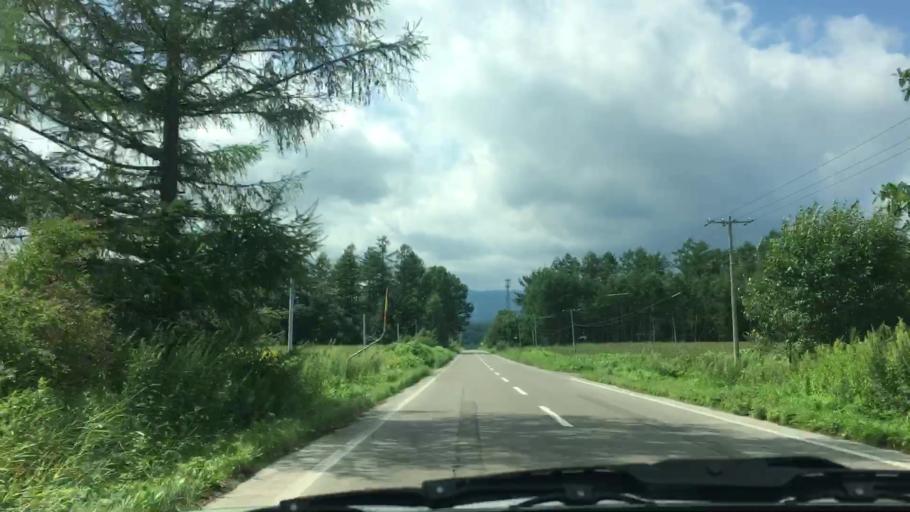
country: JP
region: Hokkaido
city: Otofuke
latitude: 43.2828
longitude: 143.3184
